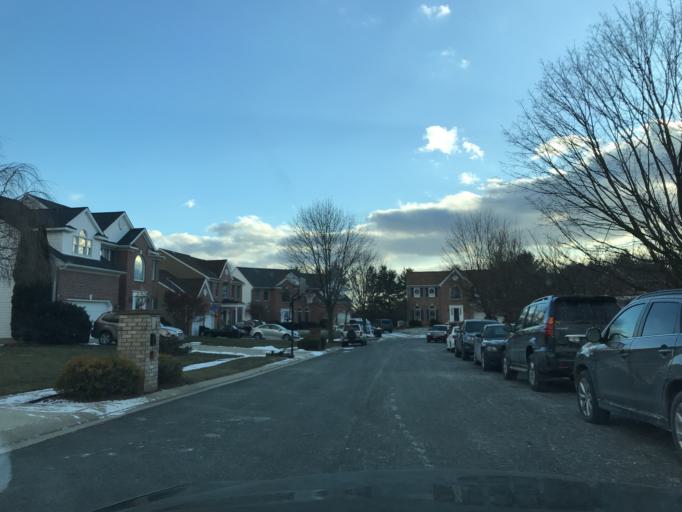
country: US
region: Maryland
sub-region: Harford County
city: Bel Air North
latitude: 39.5802
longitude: -76.3838
